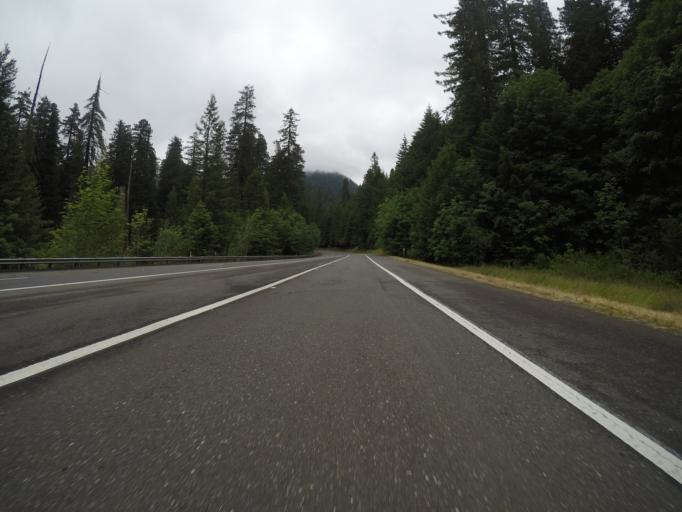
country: US
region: California
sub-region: Humboldt County
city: Rio Dell
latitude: 40.4445
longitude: -124.0397
